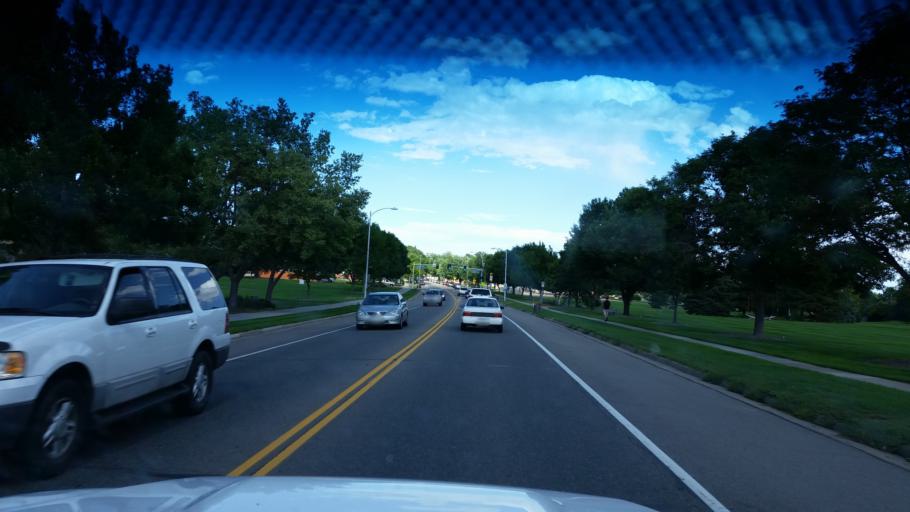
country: US
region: Colorado
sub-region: Broomfield County
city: Broomfield
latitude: 39.9226
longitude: -105.0836
